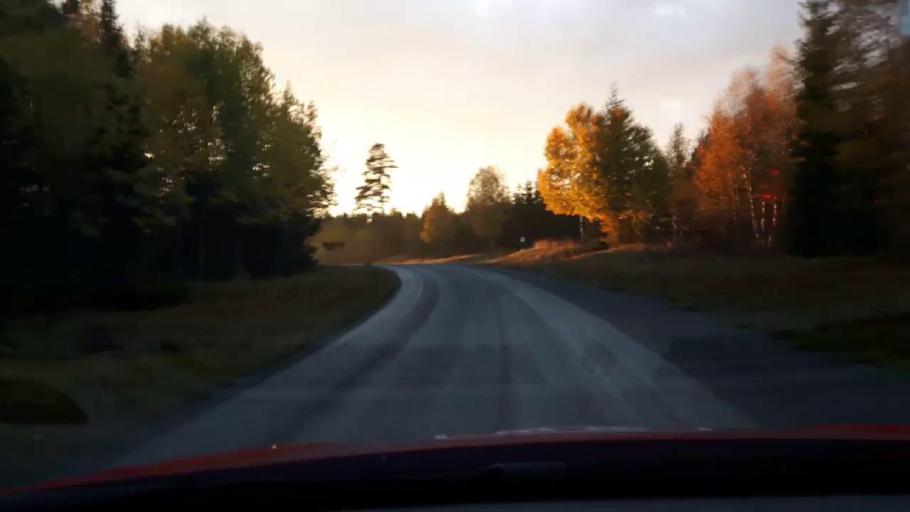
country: SE
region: Jaemtland
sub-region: OEstersunds Kommun
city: Lit
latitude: 63.2895
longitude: 14.8497
